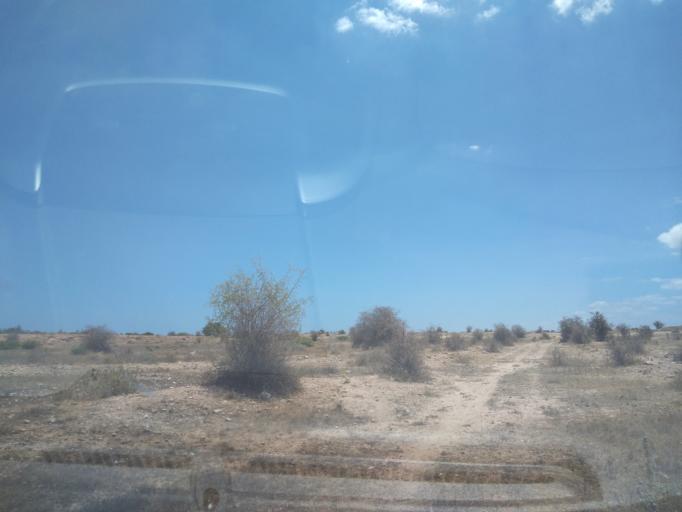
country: TN
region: Susah
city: Harqalah
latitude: 36.1729
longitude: 10.4401
